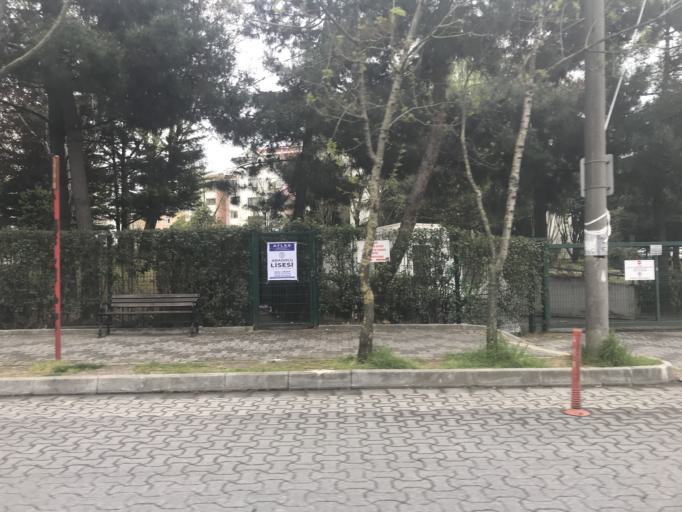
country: TR
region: Istanbul
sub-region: Atasehir
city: Atasehir
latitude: 40.9874
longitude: 29.1339
